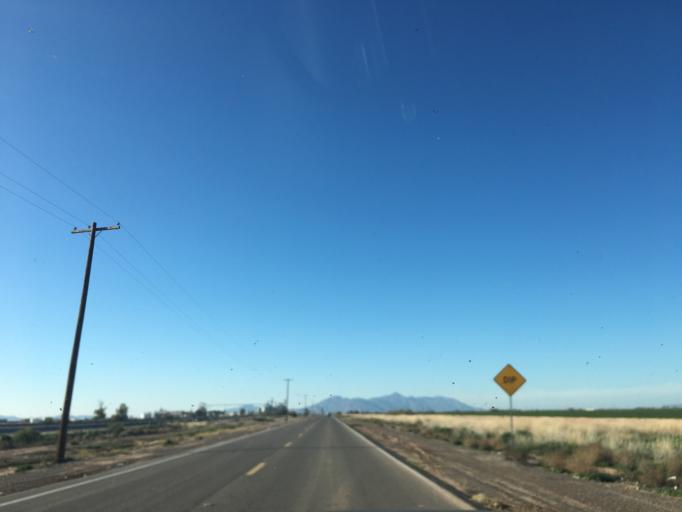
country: US
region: Arizona
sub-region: Pinal County
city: Maricopa
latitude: 33.0057
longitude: -111.9654
